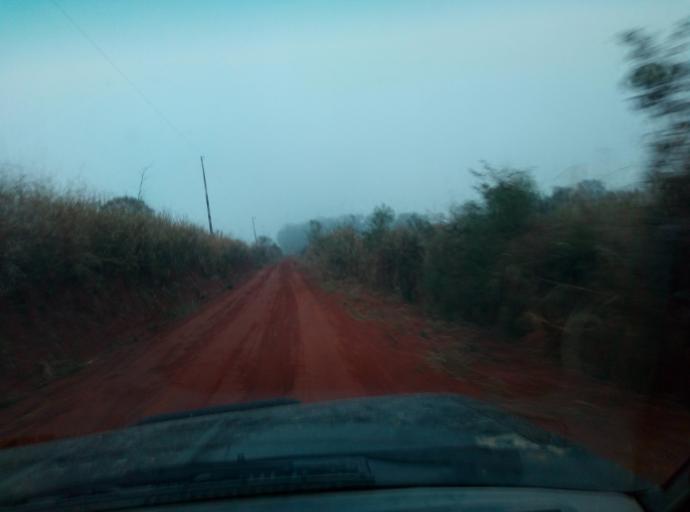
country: PY
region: Caaguazu
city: Doctor Cecilio Baez
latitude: -25.1589
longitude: -56.2648
